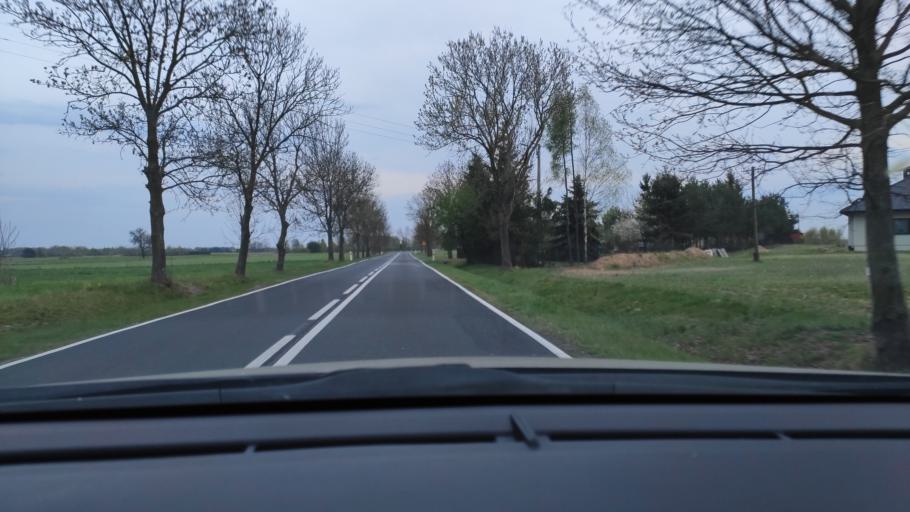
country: PL
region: Masovian Voivodeship
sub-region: Powiat zwolenski
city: Zwolen
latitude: 51.3820
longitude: 21.5593
